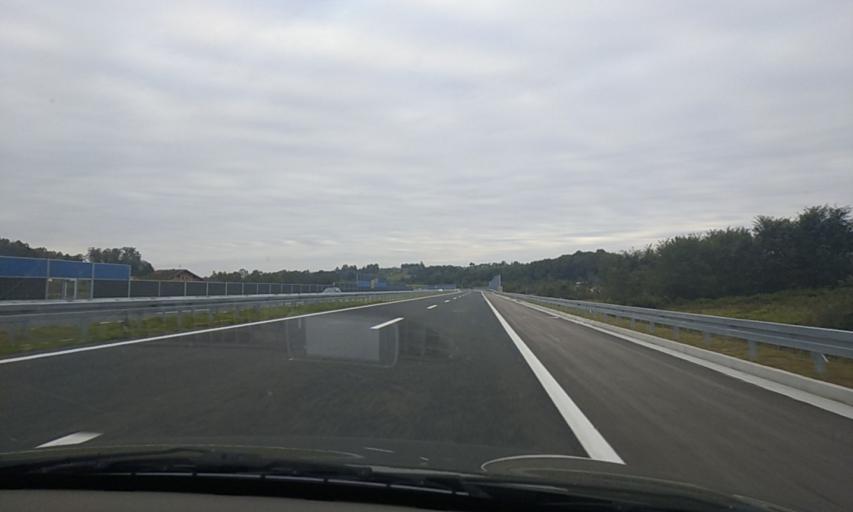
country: BA
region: Republika Srpska
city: Maglajani
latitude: 44.8629
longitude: 17.4373
